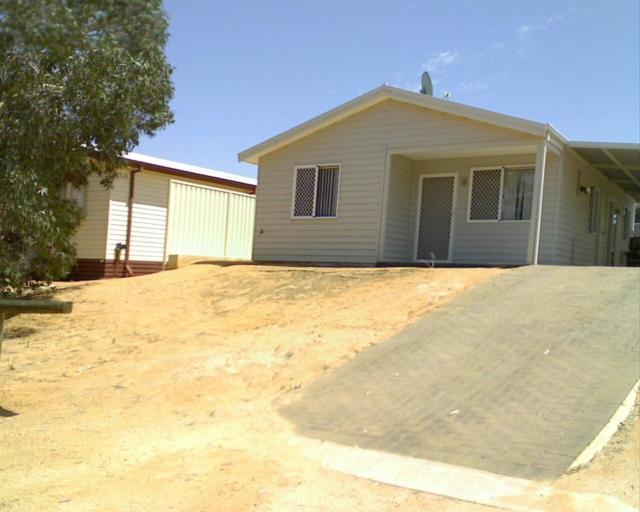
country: AU
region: Western Australia
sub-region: Merredin
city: Merredin
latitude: -30.9210
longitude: 118.2063
